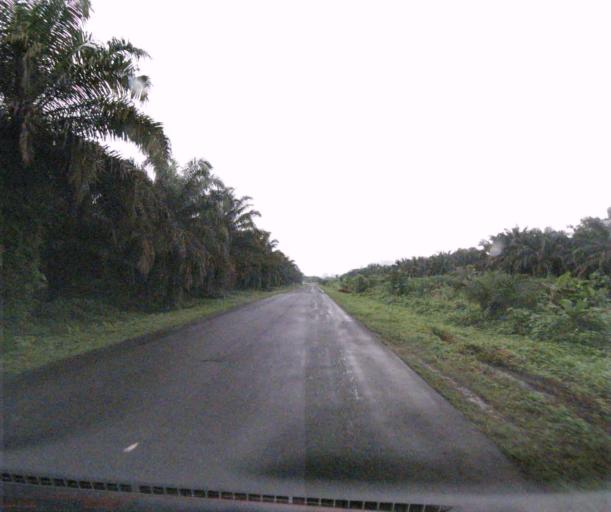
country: CM
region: South-West Province
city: Idenao
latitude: 4.1155
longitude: 8.9907
